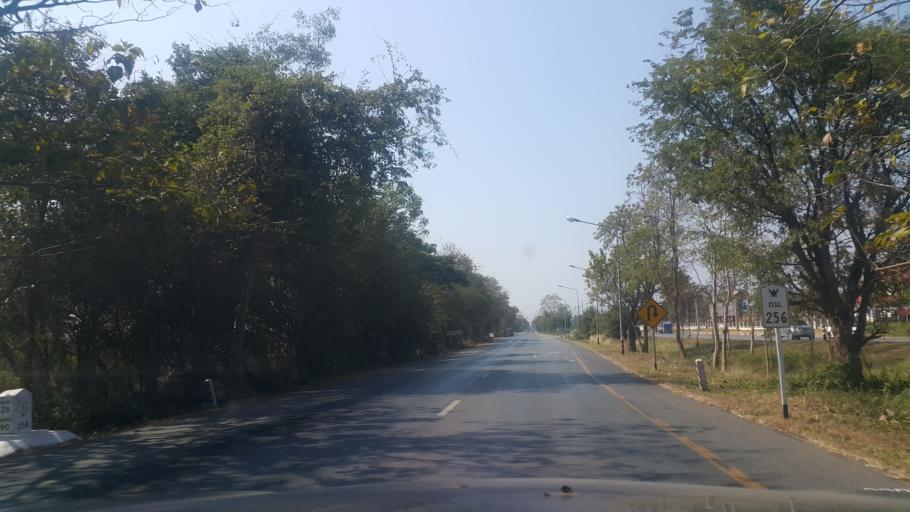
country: TH
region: Nakhon Ratchasima
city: Pak Thong Chai
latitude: 14.5917
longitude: 102.0001
